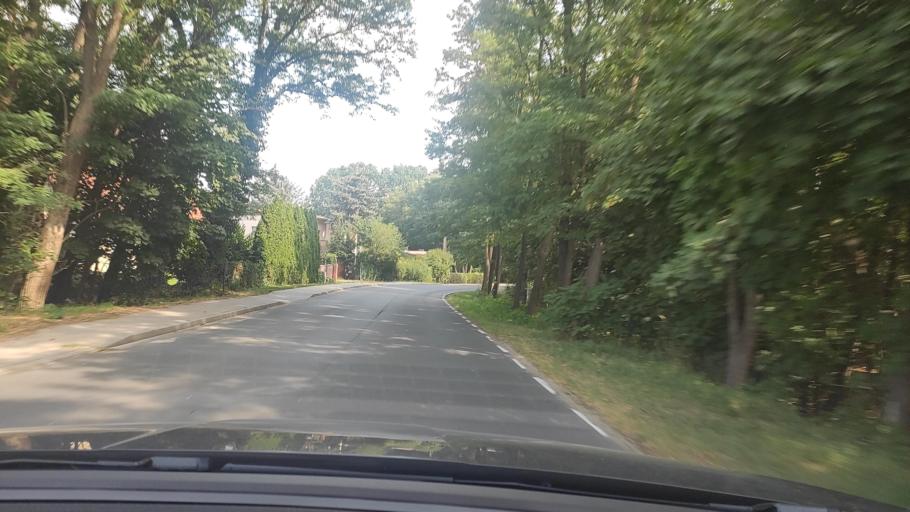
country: PL
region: Greater Poland Voivodeship
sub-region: Powiat poznanski
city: Kostrzyn
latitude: 52.4716
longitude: 17.1797
